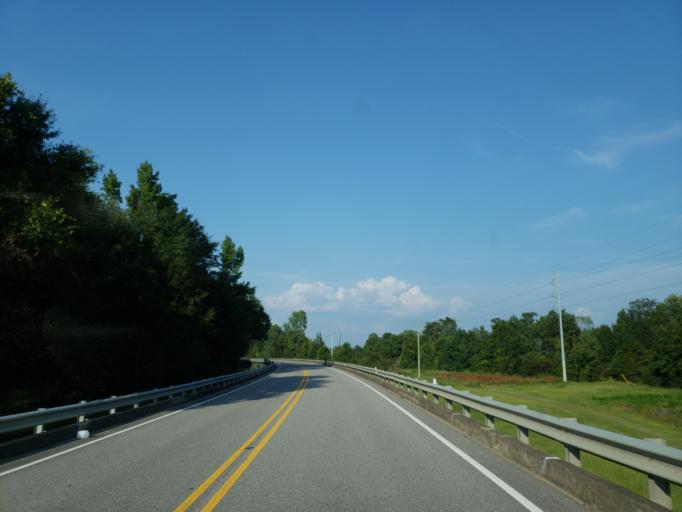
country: US
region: Alabama
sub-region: Sumter County
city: Livingston
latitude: 32.7005
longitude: -88.0912
